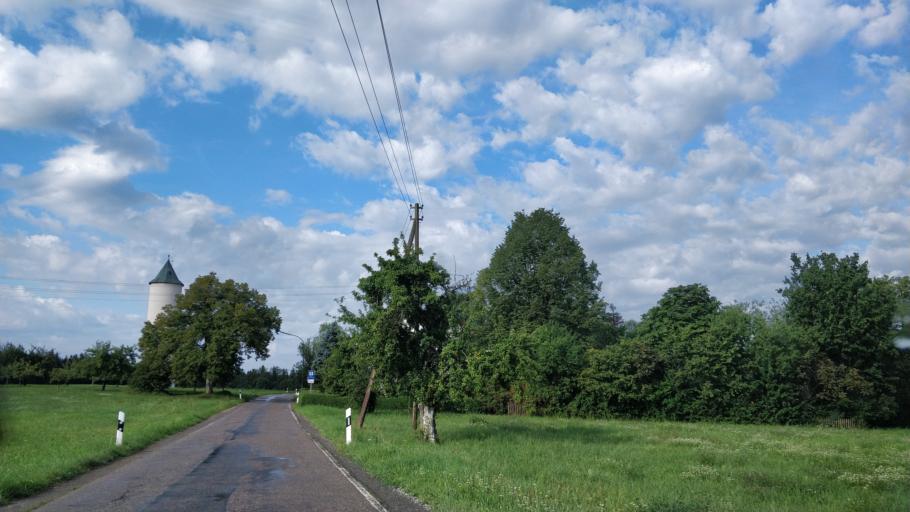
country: DE
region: Baden-Wuerttemberg
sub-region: Regierungsbezirk Stuttgart
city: Fichtenberg
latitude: 48.9774
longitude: 9.6838
